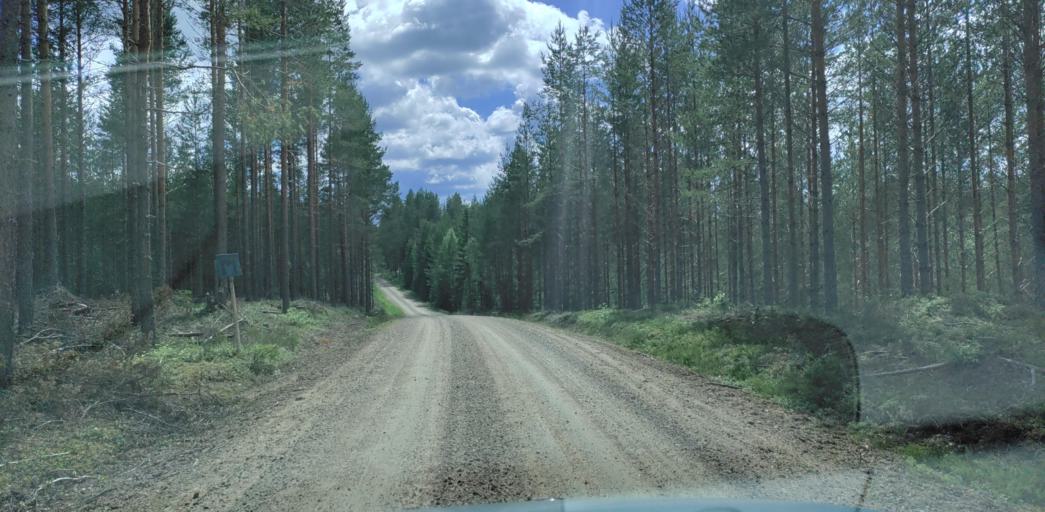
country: SE
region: Vaermland
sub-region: Hagfors Kommun
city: Ekshaerad
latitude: 60.0662
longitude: 13.2902
